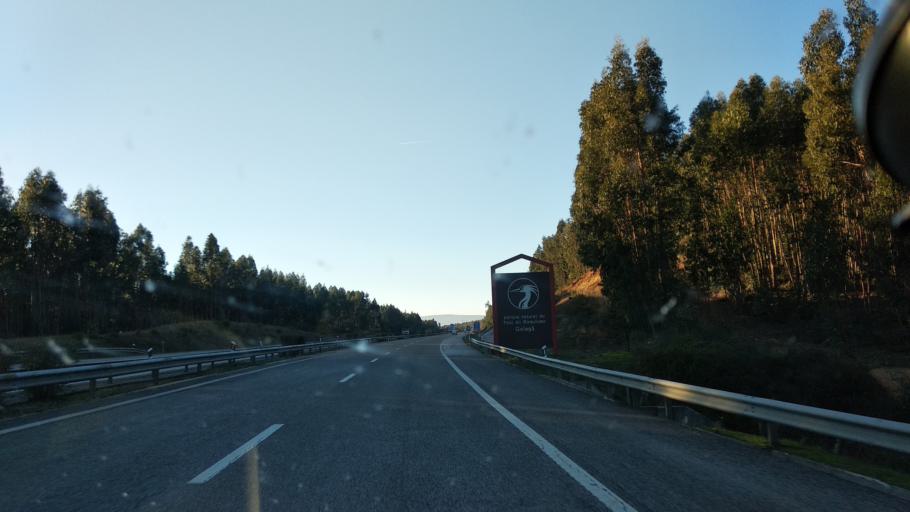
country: PT
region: Santarem
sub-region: Chamusca
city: Vila Nova da Barquinha
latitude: 39.4860
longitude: -8.4155
